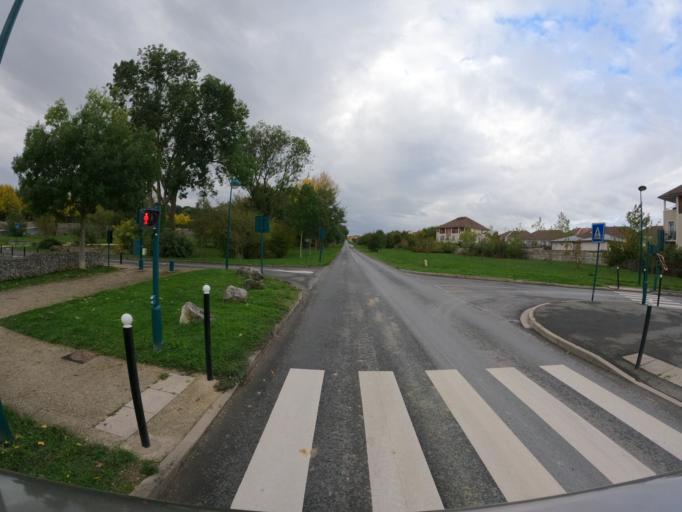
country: FR
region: Ile-de-France
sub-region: Departement de Seine-et-Marne
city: Magny-le-Hongre
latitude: 48.8709
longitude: 2.8207
